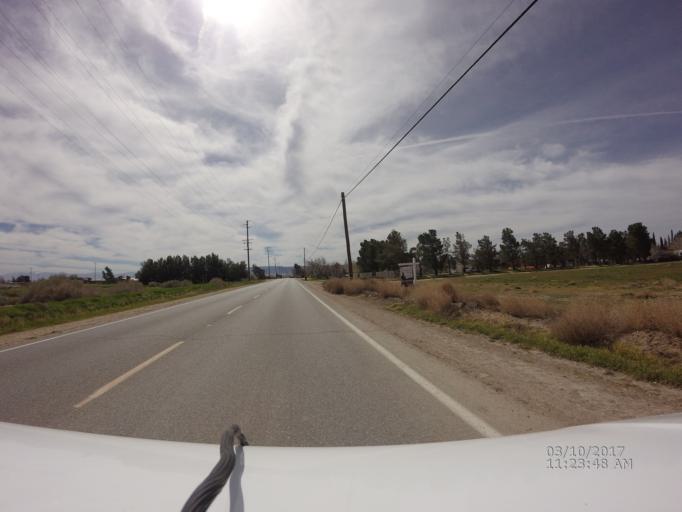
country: US
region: California
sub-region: Los Angeles County
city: Quartz Hill
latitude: 34.7523
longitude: -118.2900
